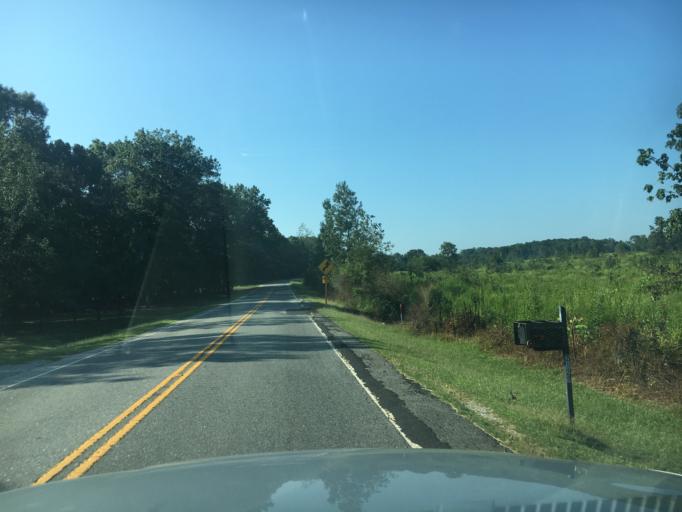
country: US
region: South Carolina
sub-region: Anderson County
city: Williamston
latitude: 34.6312
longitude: -82.3480
